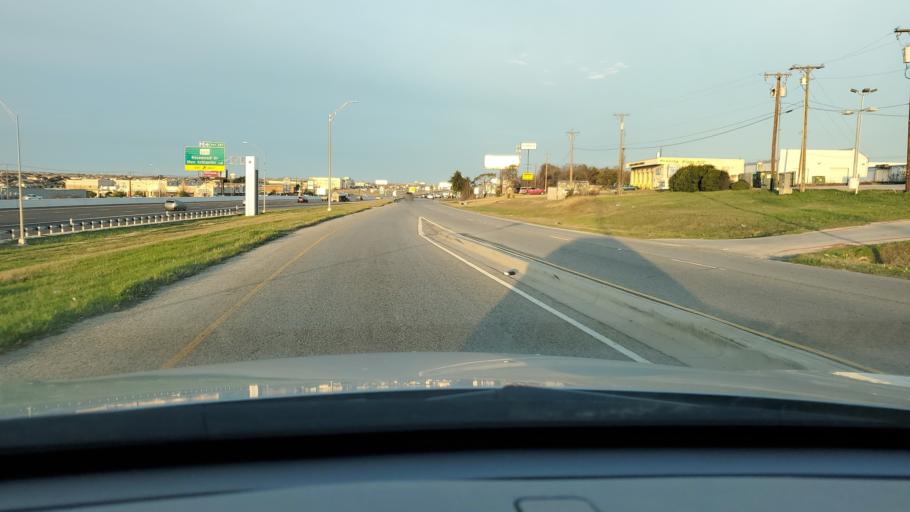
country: US
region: Texas
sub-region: Bell County
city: Harker Heights
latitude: 31.0716
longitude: -97.6711
